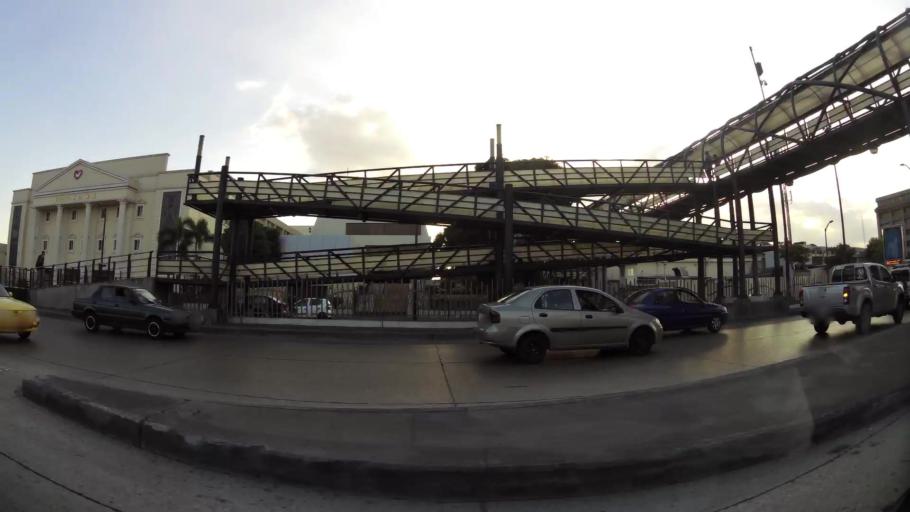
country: EC
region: Guayas
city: Eloy Alfaro
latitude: -2.1677
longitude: -79.8918
